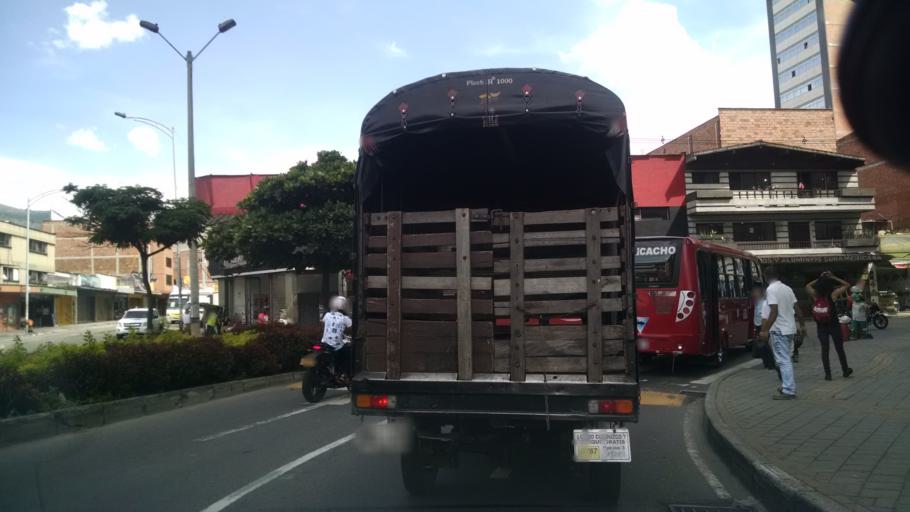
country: CO
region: Antioquia
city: Medellin
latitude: 6.2525
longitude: -75.5741
